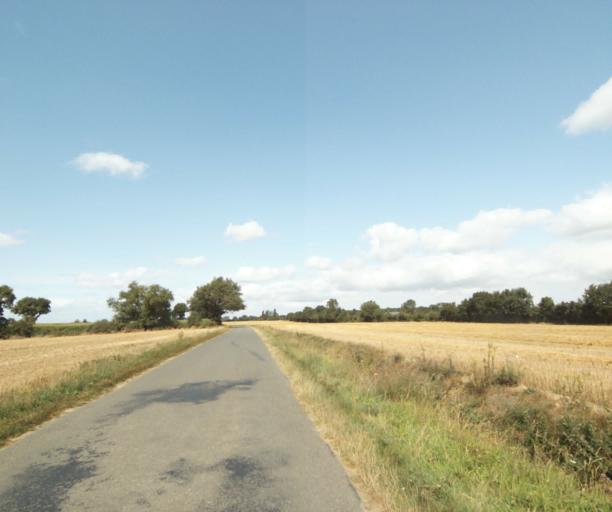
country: FR
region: Pays de la Loire
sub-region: Departement de la Sarthe
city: Sable-sur-Sarthe
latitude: 47.8493
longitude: -0.3892
